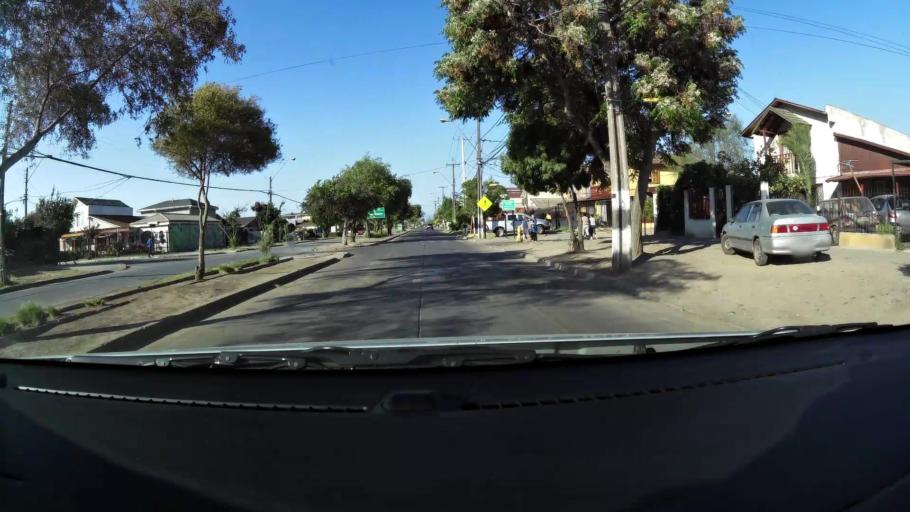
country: CL
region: Santiago Metropolitan
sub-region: Provincia de Maipo
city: San Bernardo
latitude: -33.5439
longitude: -70.7730
